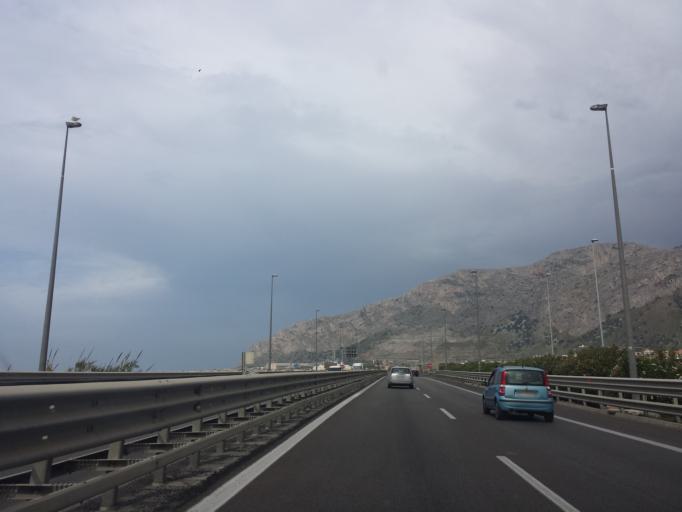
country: IT
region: Sicily
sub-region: Palermo
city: Capaci
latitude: 38.1779
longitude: 13.2235
